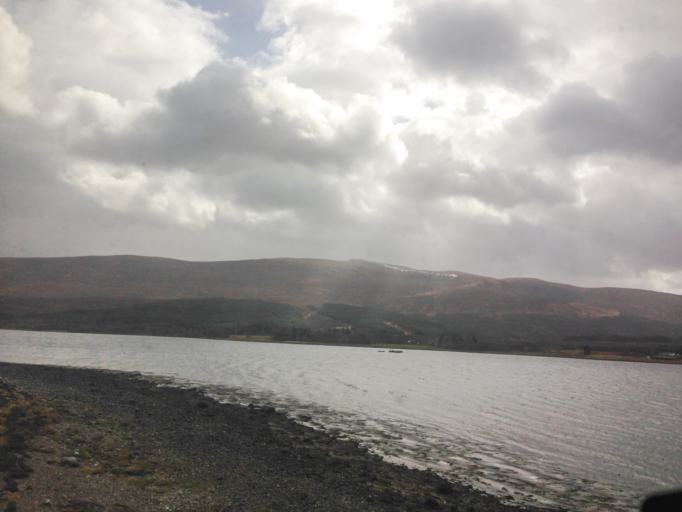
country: GB
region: Scotland
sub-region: Highland
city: Fort William
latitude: 56.8544
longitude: -5.2655
